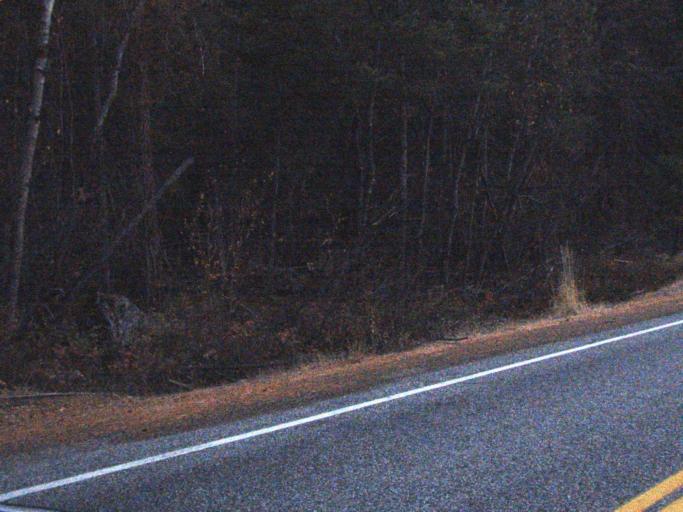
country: US
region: Washington
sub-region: Ferry County
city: Republic
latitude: 48.4819
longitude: -118.7309
